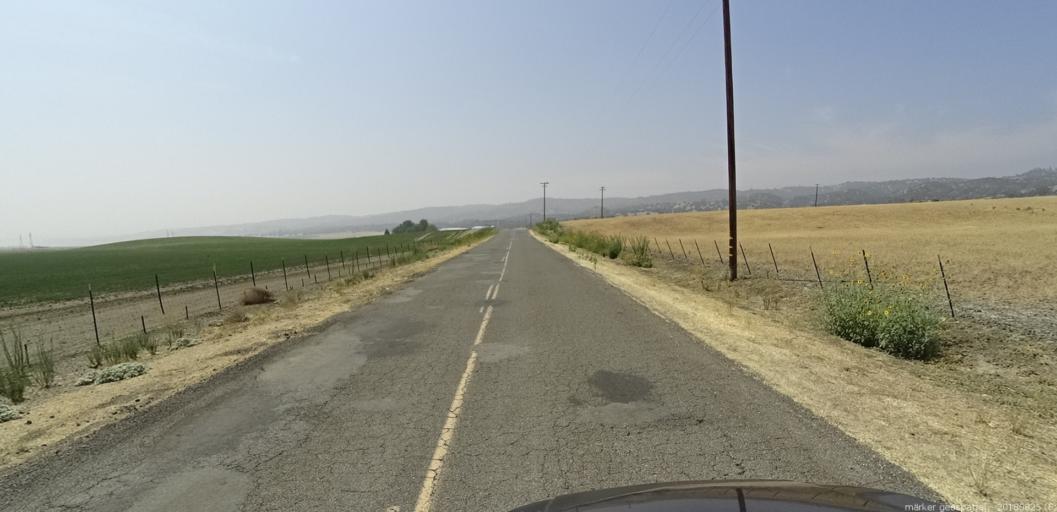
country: US
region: California
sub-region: San Luis Obispo County
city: Shandon
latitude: 35.8385
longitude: -120.3816
